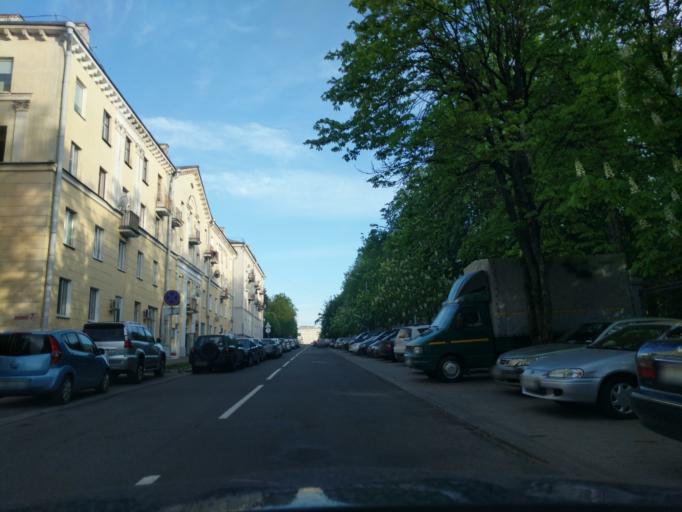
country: BY
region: Minsk
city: Minsk
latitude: 53.9060
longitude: 27.5742
